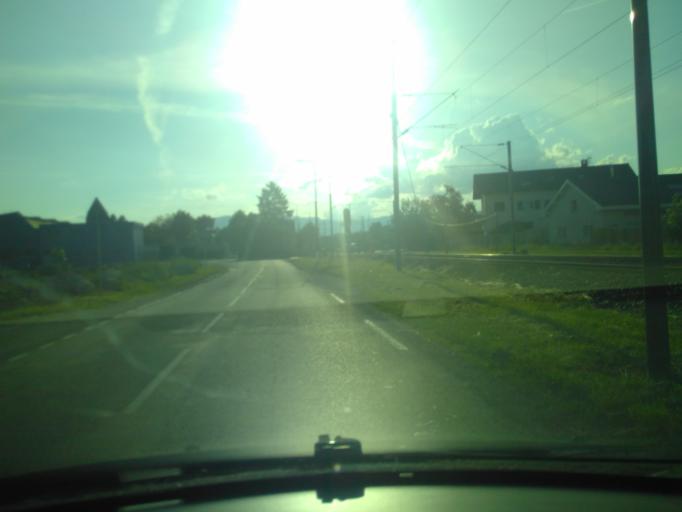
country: FR
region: Rhone-Alpes
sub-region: Departement de la Haute-Savoie
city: Saint-Julien-en-Genevois
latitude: 46.1418
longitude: 6.0930
